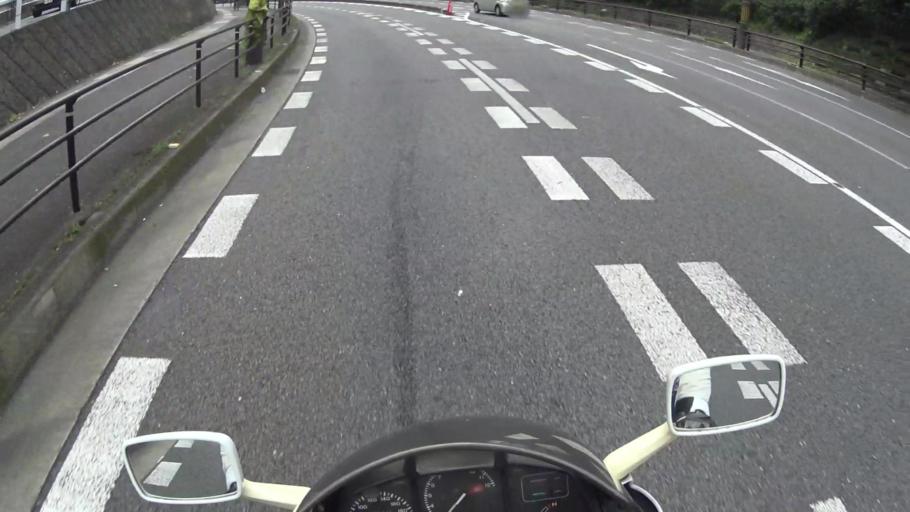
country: JP
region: Kyoto
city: Kyoto
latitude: 35.0046
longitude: 135.7910
